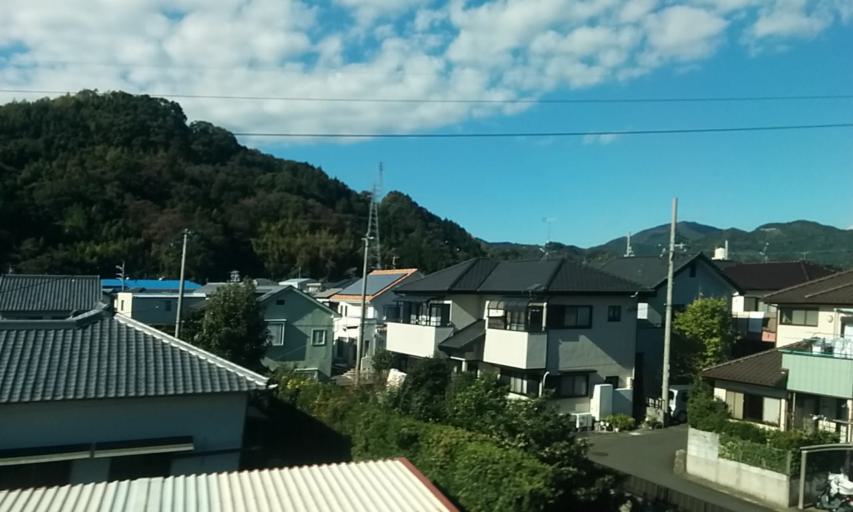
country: JP
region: Shizuoka
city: Shizuoka-shi
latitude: 34.9369
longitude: 138.3629
